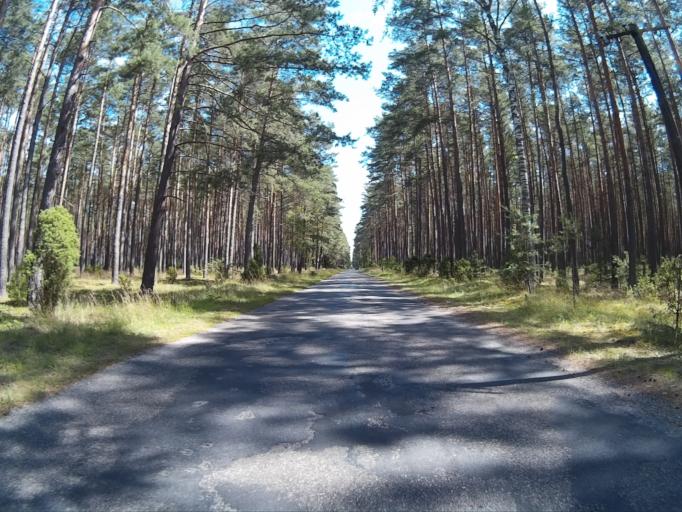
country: PL
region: Kujawsko-Pomorskie
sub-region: Powiat tucholski
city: Tuchola
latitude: 53.6759
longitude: 17.9251
